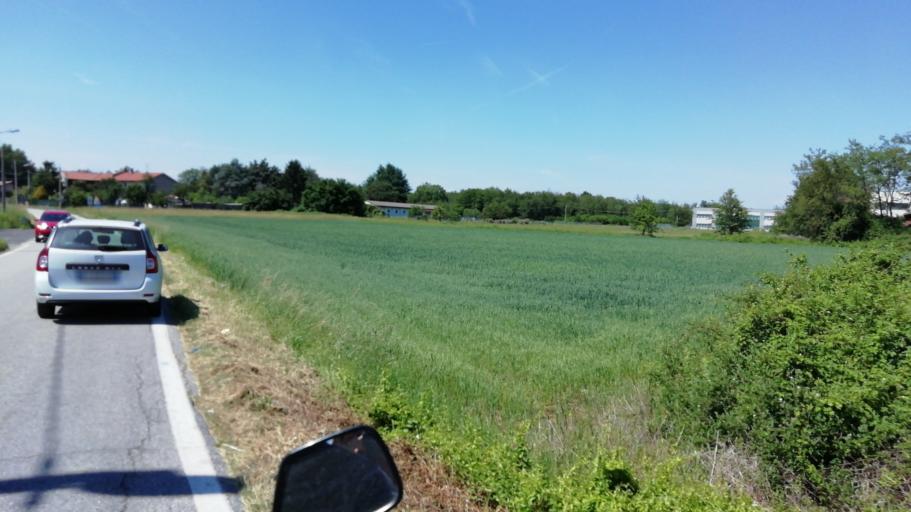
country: IT
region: Lombardy
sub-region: Provincia di Varese
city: Lonate Pozzolo
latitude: 45.6026
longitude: 8.7457
